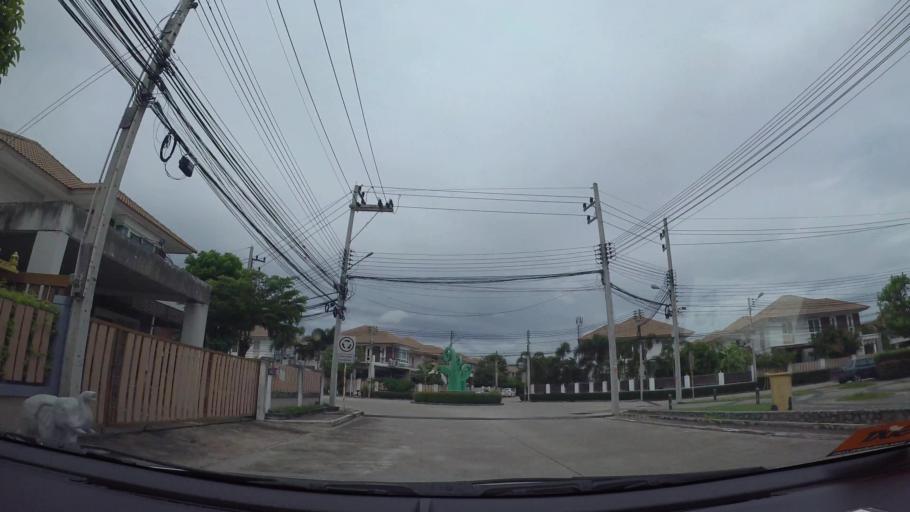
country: TH
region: Chon Buri
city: Si Racha
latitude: 13.1441
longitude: 100.9829
